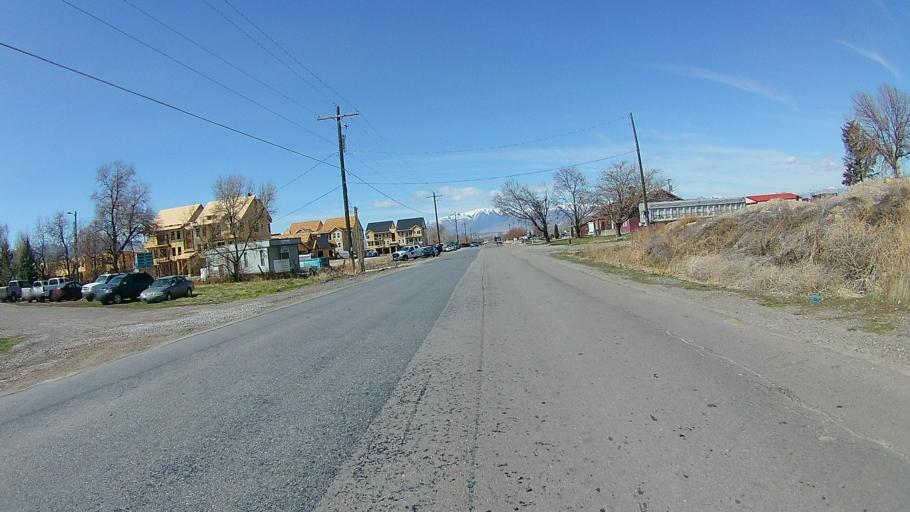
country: US
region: Utah
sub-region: Utah County
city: American Fork
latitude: 40.3728
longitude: -111.8168
